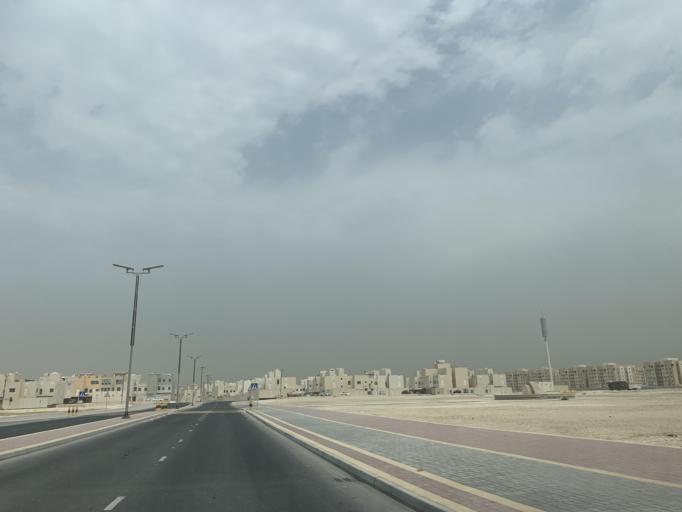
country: BH
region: Northern
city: Madinat `Isa
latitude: 26.1722
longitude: 50.5154
